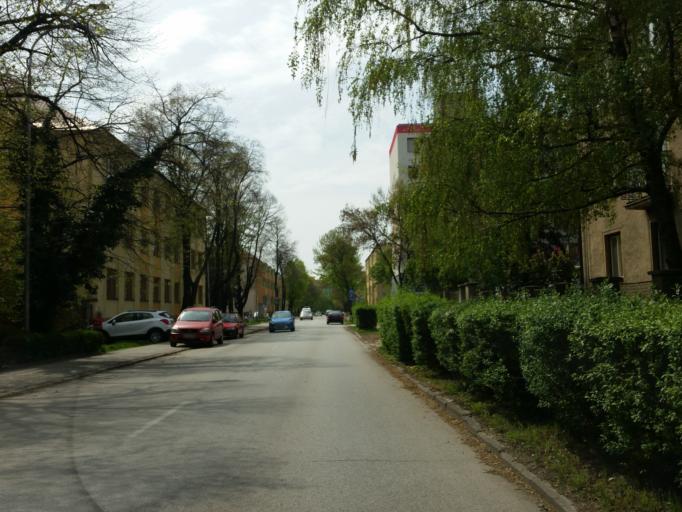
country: SK
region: Trnavsky
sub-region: Okres Galanta
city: Galanta
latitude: 48.2884
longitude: 17.7352
